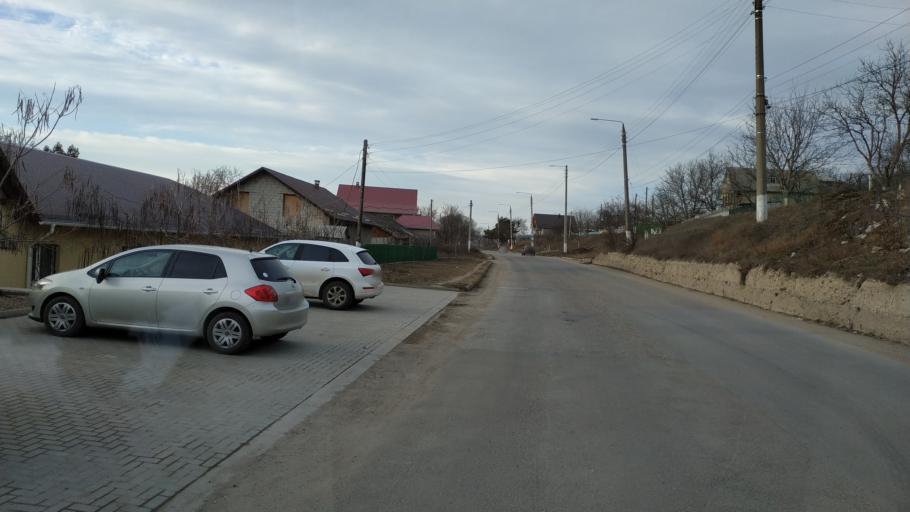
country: MD
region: Nisporeni
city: Nisporeni
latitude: 47.0883
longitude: 28.1821
